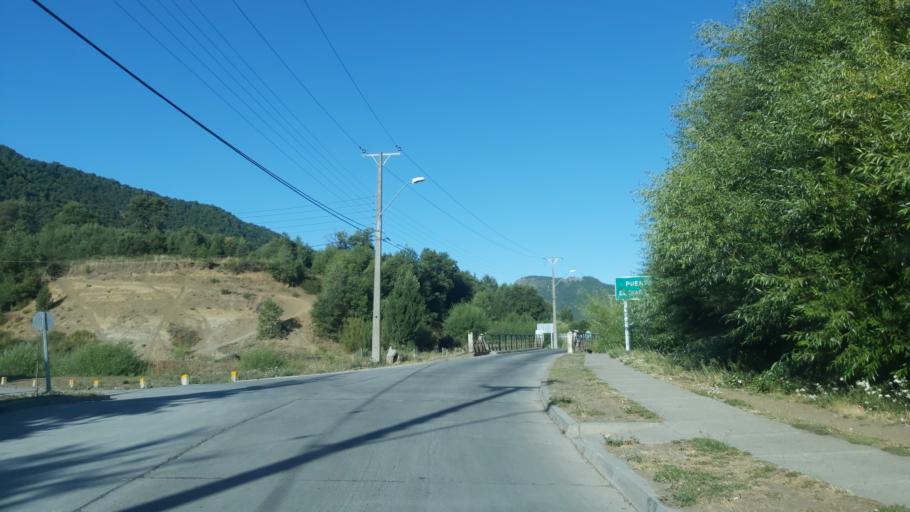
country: AR
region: Neuquen
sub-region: Departamento de Loncopue
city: Loncopue
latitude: -38.4484
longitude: -71.3667
